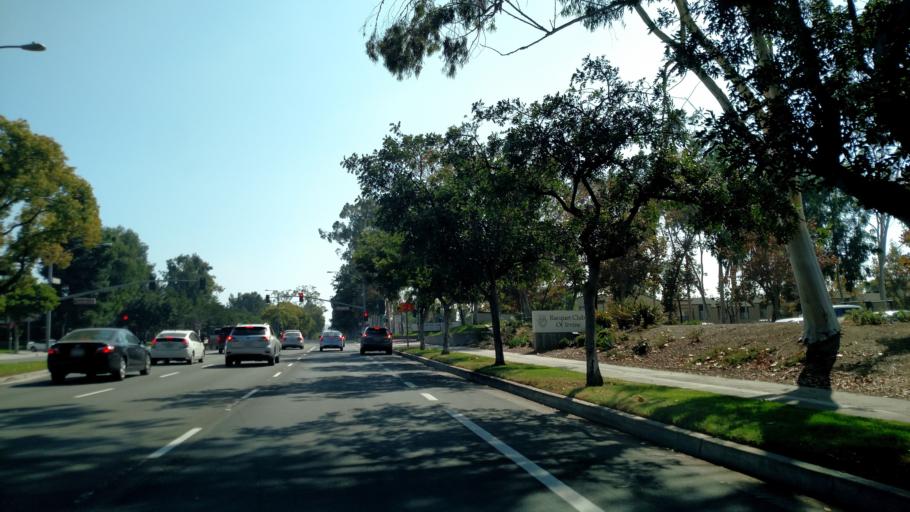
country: US
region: California
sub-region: Orange County
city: Irvine
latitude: 33.6630
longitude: -117.8277
